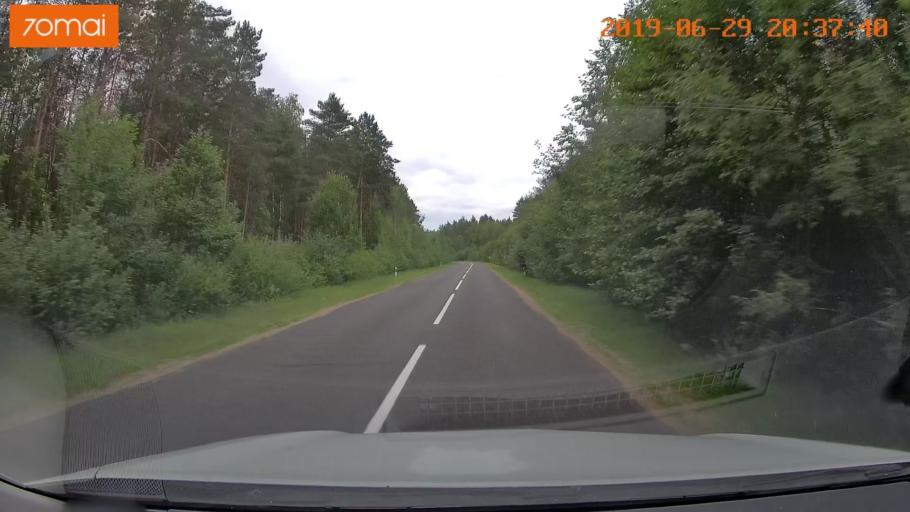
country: BY
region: Brest
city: Hantsavichy
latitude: 52.5408
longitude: 26.3653
